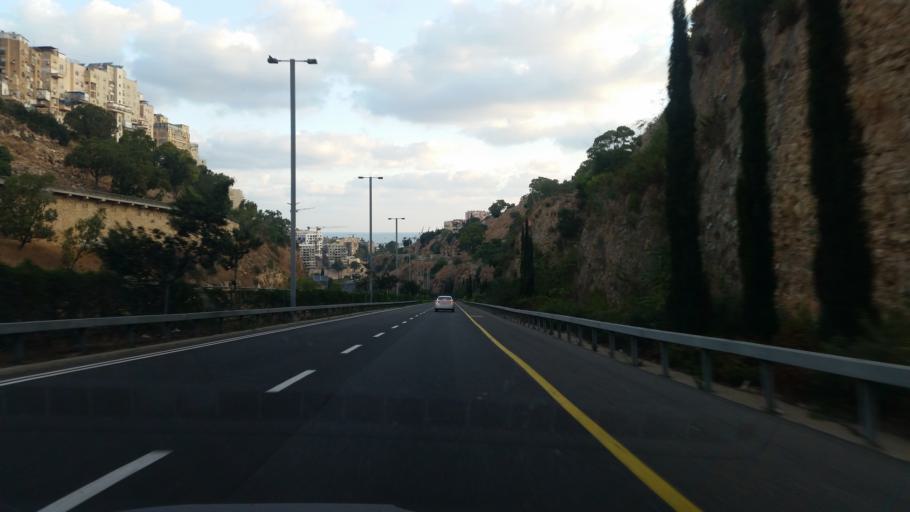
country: IL
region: Haifa
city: Haifa
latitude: 32.7953
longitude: 35.0044
